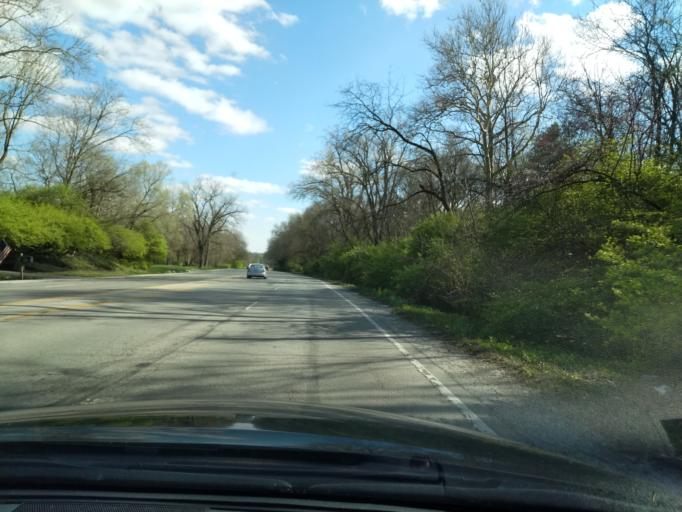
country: US
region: Indiana
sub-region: Marion County
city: Meridian Hills
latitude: 39.8773
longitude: -86.1579
